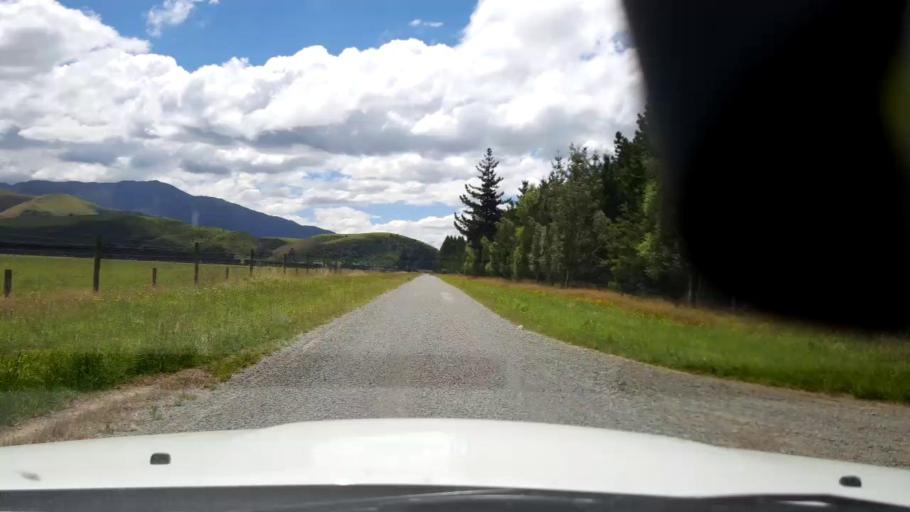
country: NZ
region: Canterbury
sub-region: Timaru District
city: Pleasant Point
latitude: -43.9659
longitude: 171.2266
